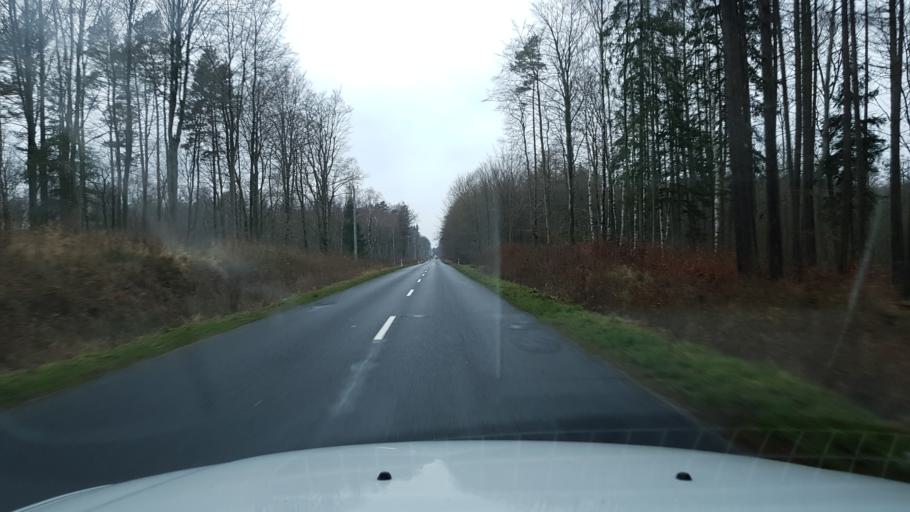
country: PL
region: West Pomeranian Voivodeship
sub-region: Powiat gryficki
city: Trzebiatow
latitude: 54.0562
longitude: 15.3505
